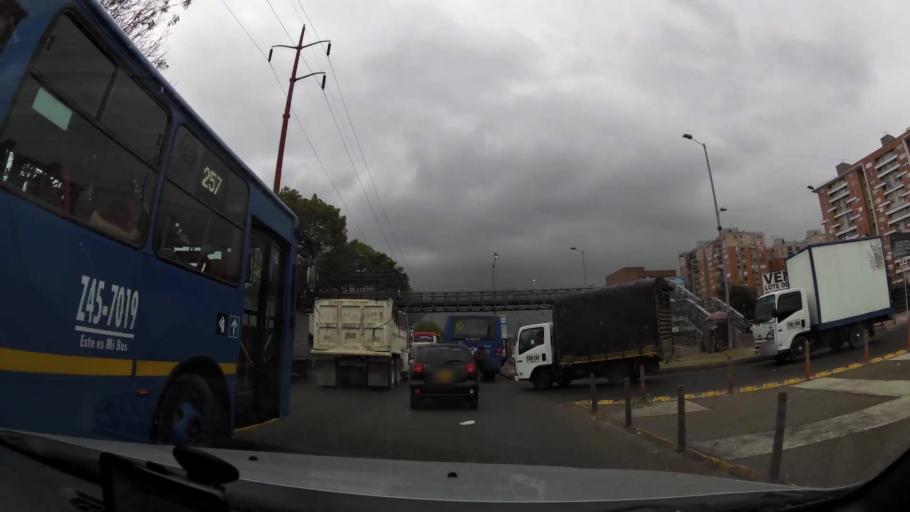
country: CO
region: Bogota D.C.
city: Bogota
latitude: 4.6533
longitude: -74.1303
